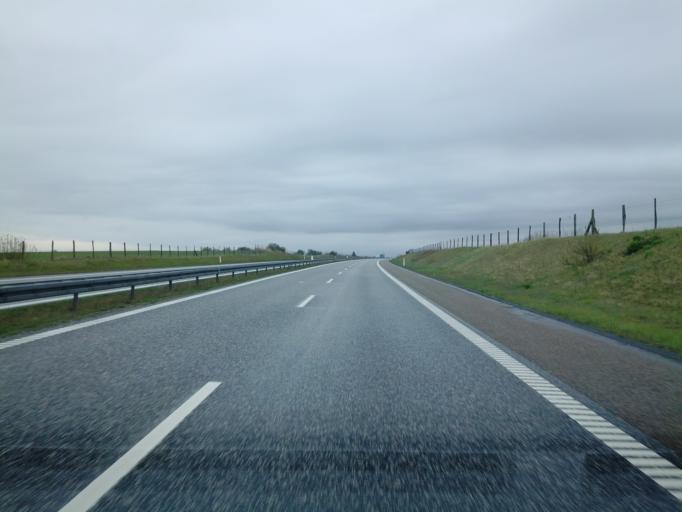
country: DK
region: North Denmark
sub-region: Frederikshavn Kommune
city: Saeby
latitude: 57.2774
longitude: 10.3847
